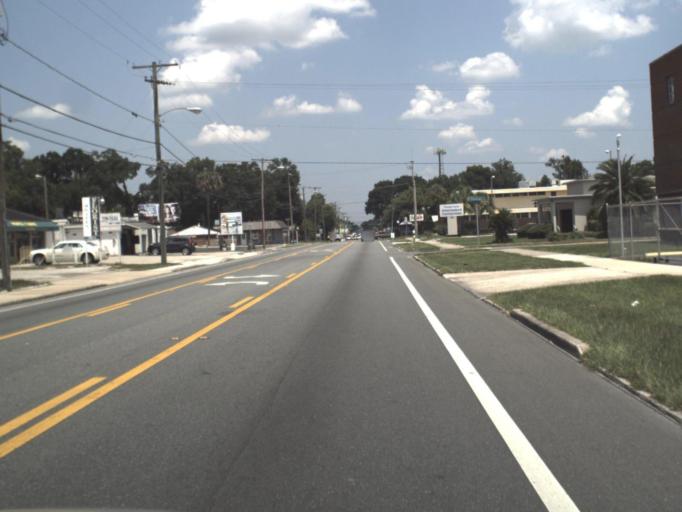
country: US
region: Florida
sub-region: Hillsborough County
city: Tampa
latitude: 27.9910
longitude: -82.4511
